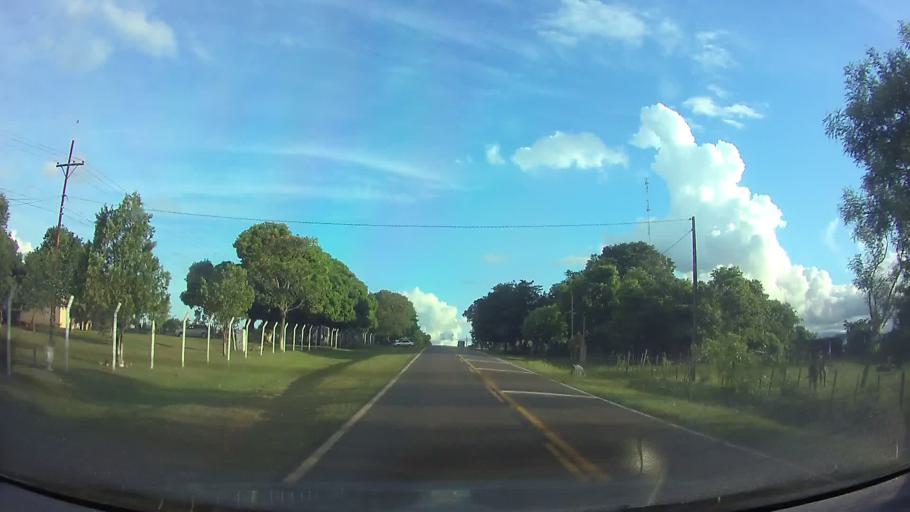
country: PY
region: Paraguari
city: Acahay
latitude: -25.9498
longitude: -57.0939
